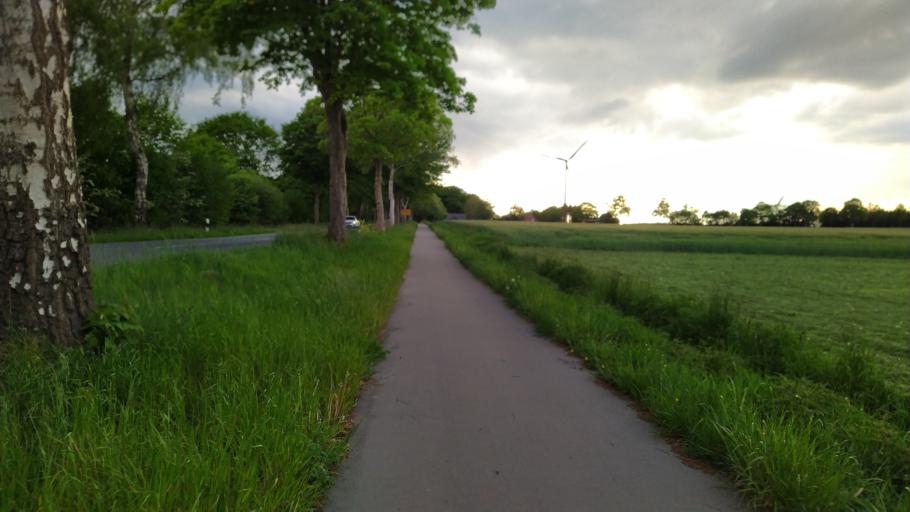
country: DE
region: Lower Saxony
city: Ahlerstedt
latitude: 53.3954
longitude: 9.4088
